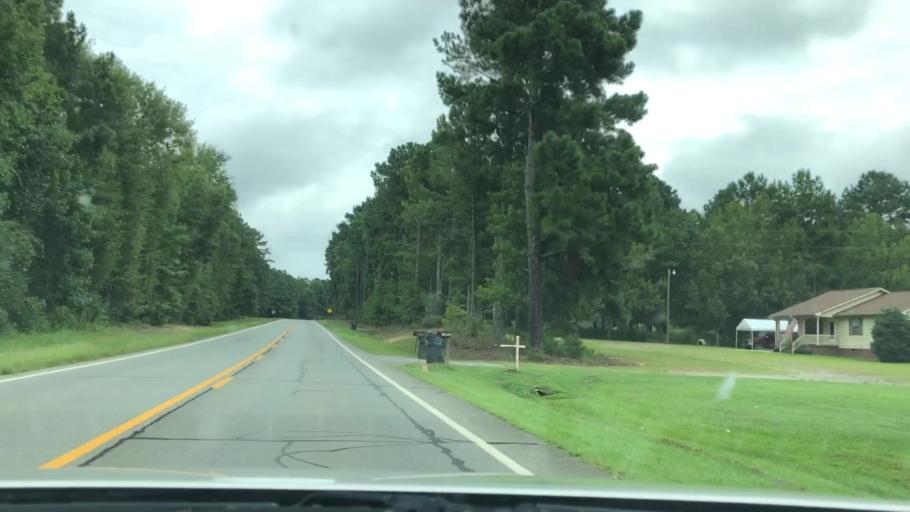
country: US
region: Georgia
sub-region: Pike County
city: Zebulon
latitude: 33.0993
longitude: -84.4255
